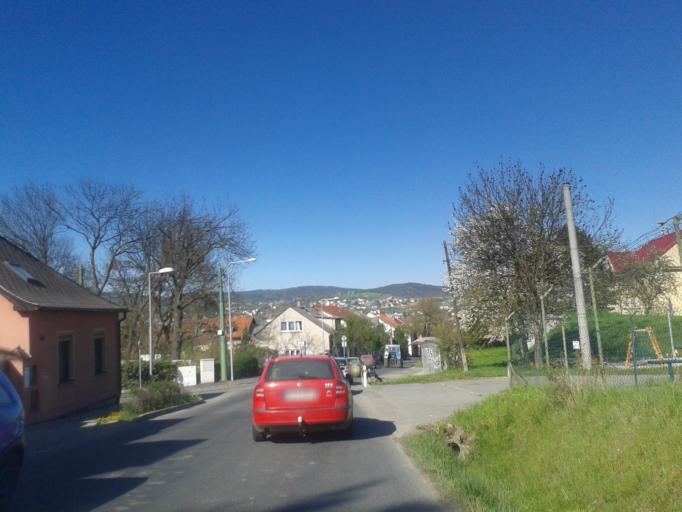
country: CZ
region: Central Bohemia
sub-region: Okres Beroun
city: Beroun
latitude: 49.9530
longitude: 14.0710
